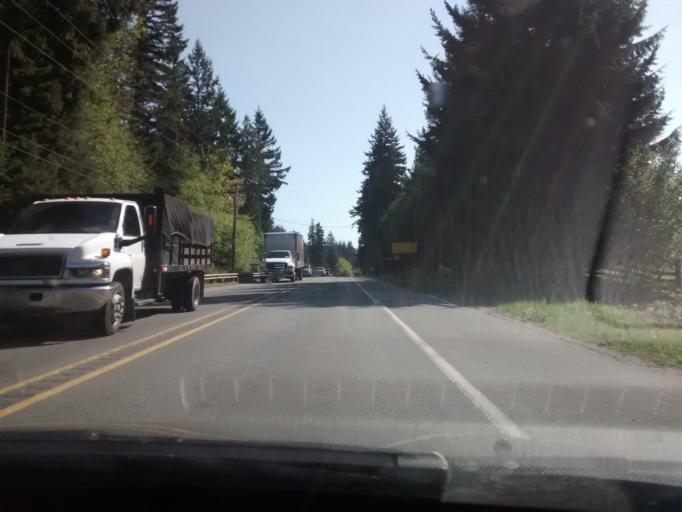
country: US
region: Washington
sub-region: Kitsap County
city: Kingston
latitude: 47.8095
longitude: -122.5267
